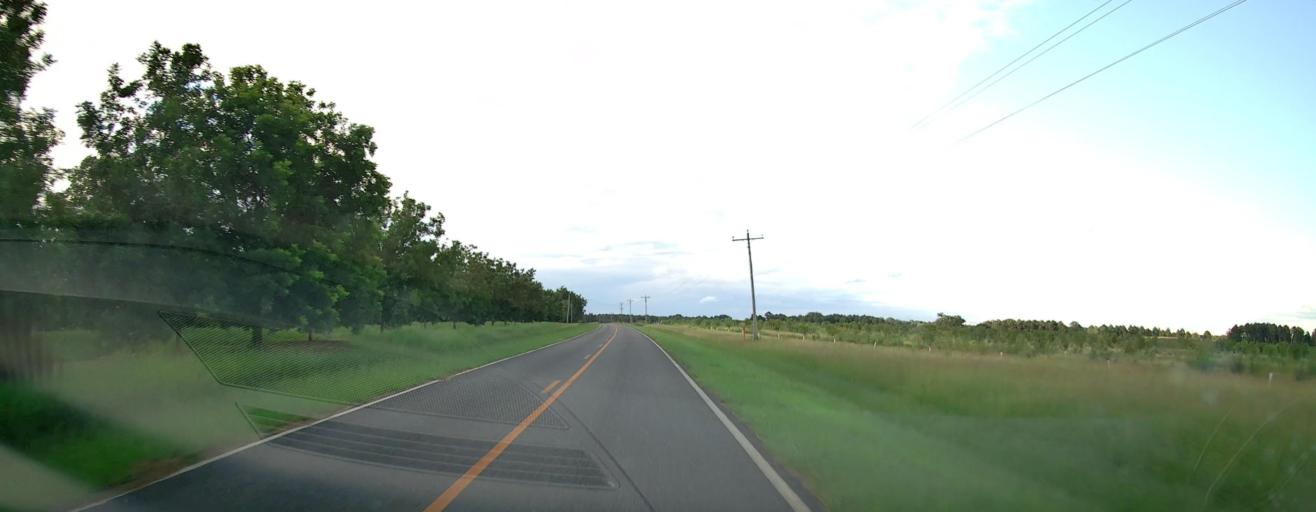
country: US
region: Georgia
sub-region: Pulaski County
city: Hawkinsville
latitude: 32.3147
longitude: -83.5524
